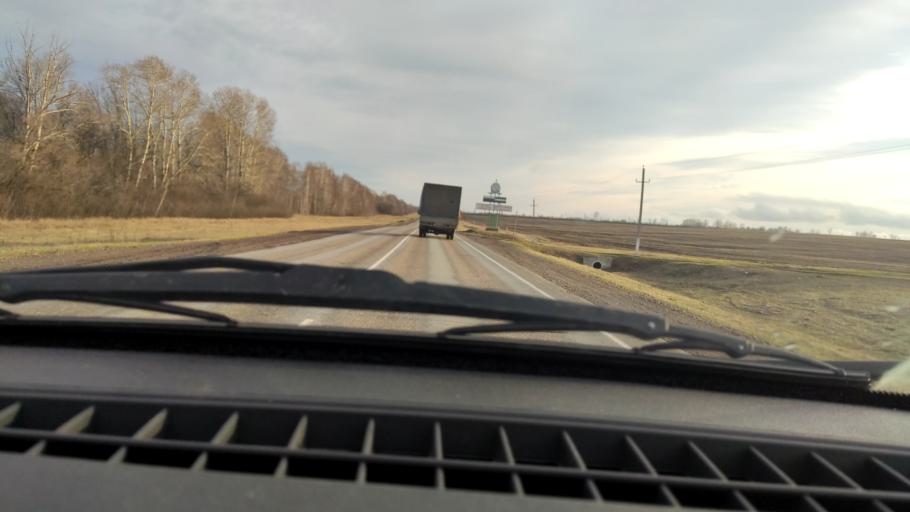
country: RU
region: Bashkortostan
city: Davlekanovo
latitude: 54.3416
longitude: 55.1730
